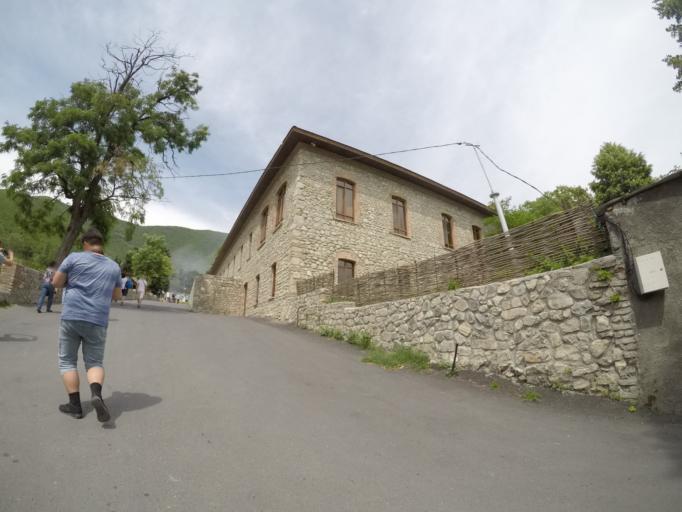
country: AZ
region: Shaki City
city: Sheki
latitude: 41.2040
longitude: 47.1966
